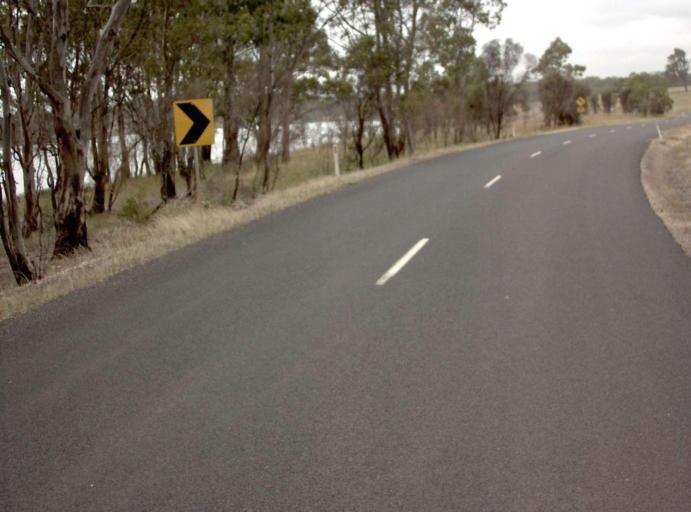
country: AU
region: Victoria
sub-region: Wellington
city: Heyfield
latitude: -37.8989
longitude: 146.7391
